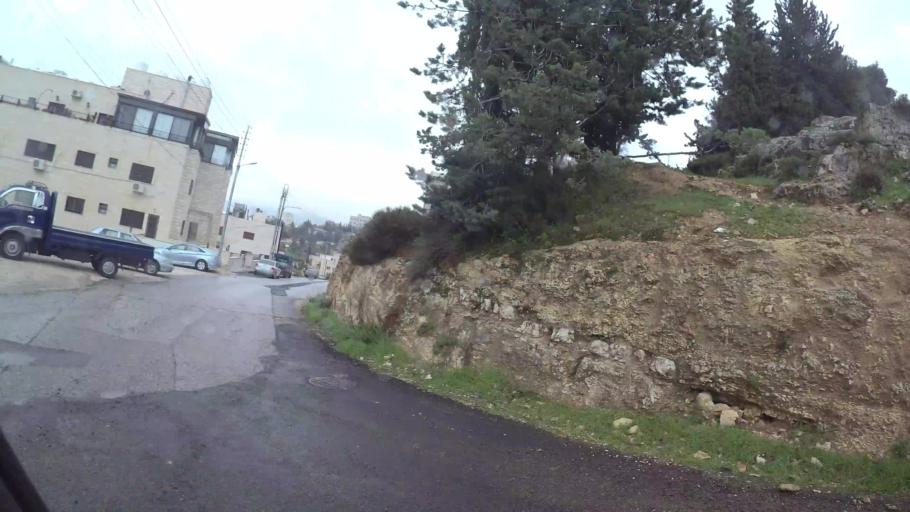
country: JO
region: Amman
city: Al Jubayhah
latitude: 32.0260
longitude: 35.8294
